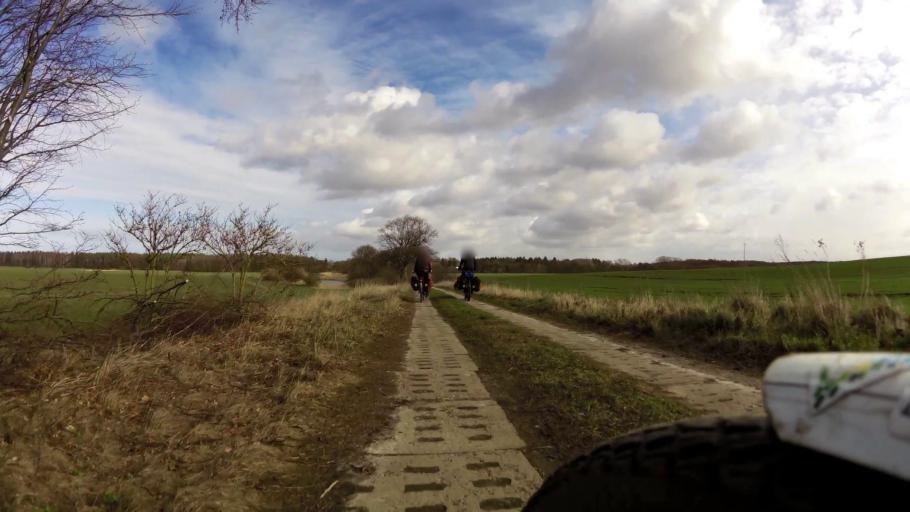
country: PL
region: West Pomeranian Voivodeship
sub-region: Powiat kamienski
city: Dziwnow
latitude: 54.0001
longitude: 14.7807
